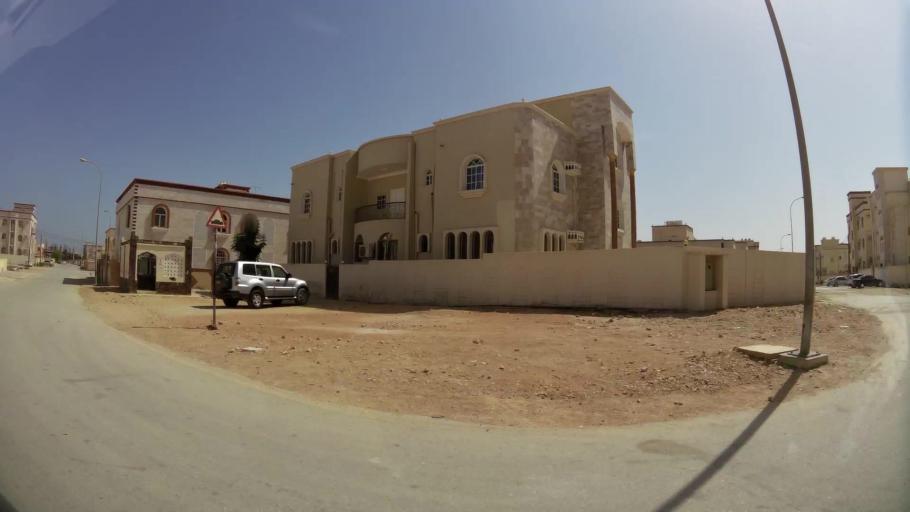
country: OM
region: Zufar
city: Salalah
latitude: 17.0495
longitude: 54.1603
